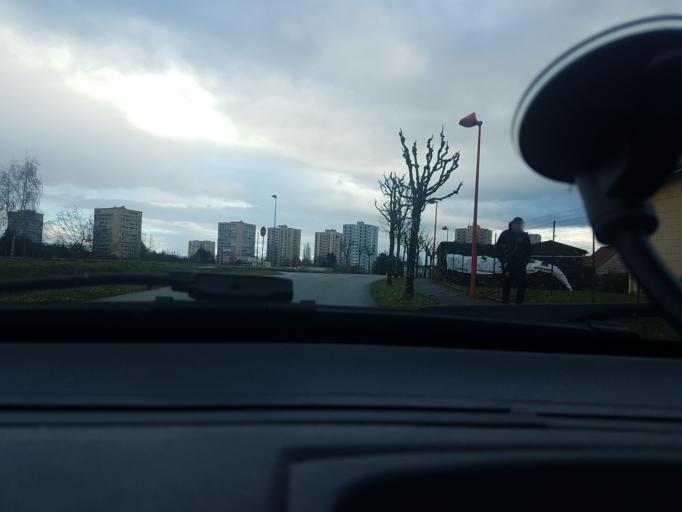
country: FR
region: Franche-Comte
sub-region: Territoire de Belfort
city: Bavilliers
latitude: 47.6274
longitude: 6.8357
